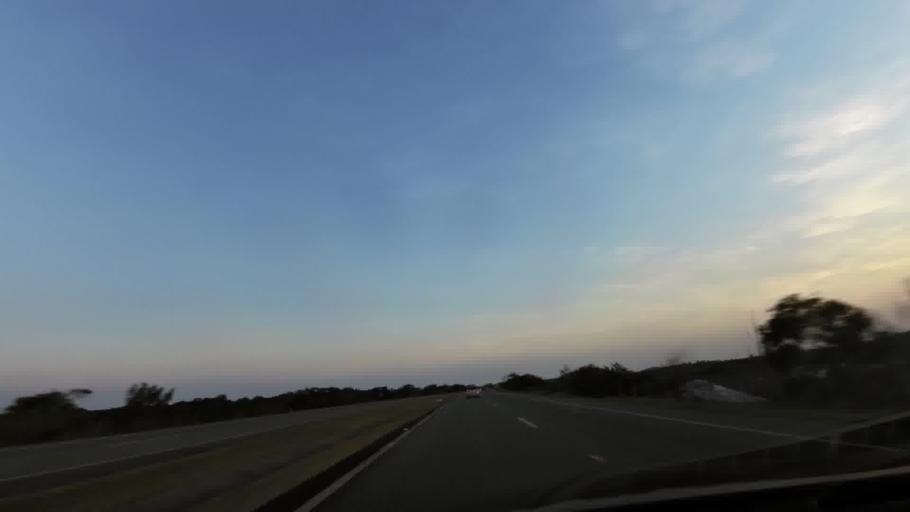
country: BR
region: Espirito Santo
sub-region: Guarapari
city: Guarapari
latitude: -20.6100
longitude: -40.4281
